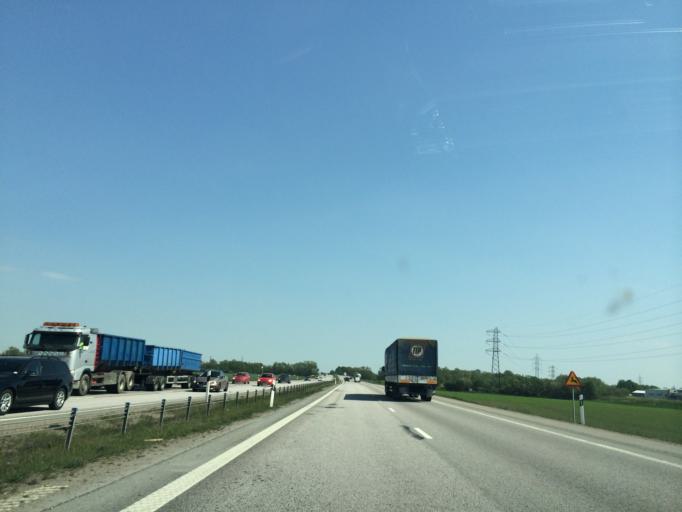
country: SE
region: OEstergoetland
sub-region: Linkopings Kommun
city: Linkoping
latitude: 58.4348
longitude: 15.6109
